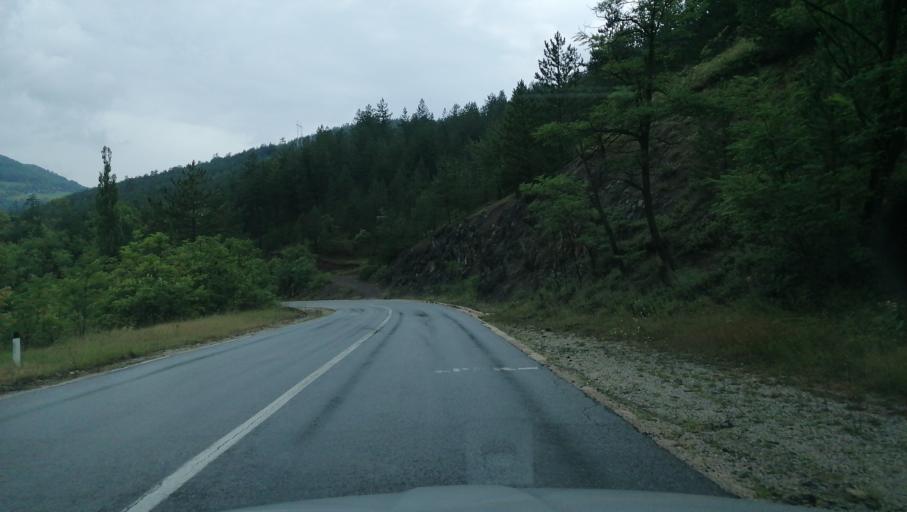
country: RS
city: Durici
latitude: 43.8095
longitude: 19.5116
